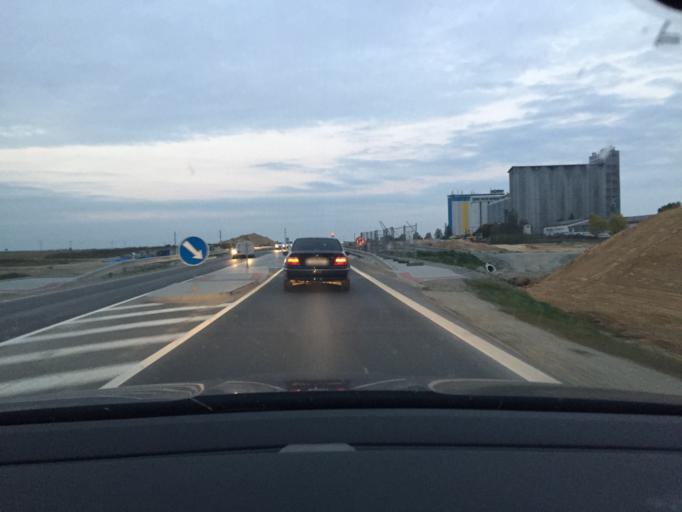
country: CZ
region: Jihocesky
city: Dolni Bukovsko
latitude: 49.1417
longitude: 14.6196
